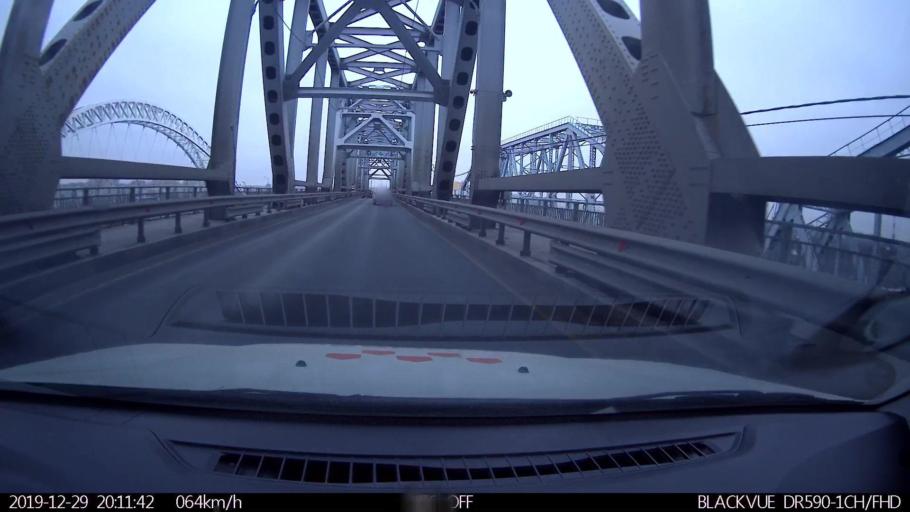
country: RU
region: Nizjnij Novgorod
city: Neklyudovo
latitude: 56.3544
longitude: 43.9250
